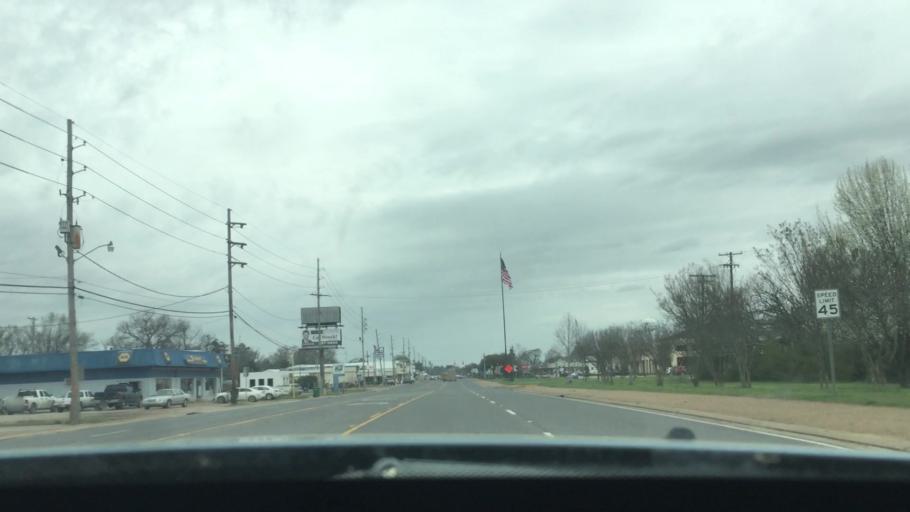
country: US
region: Louisiana
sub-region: Franklin Parish
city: Winnsboro
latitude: 32.1613
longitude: -91.7185
